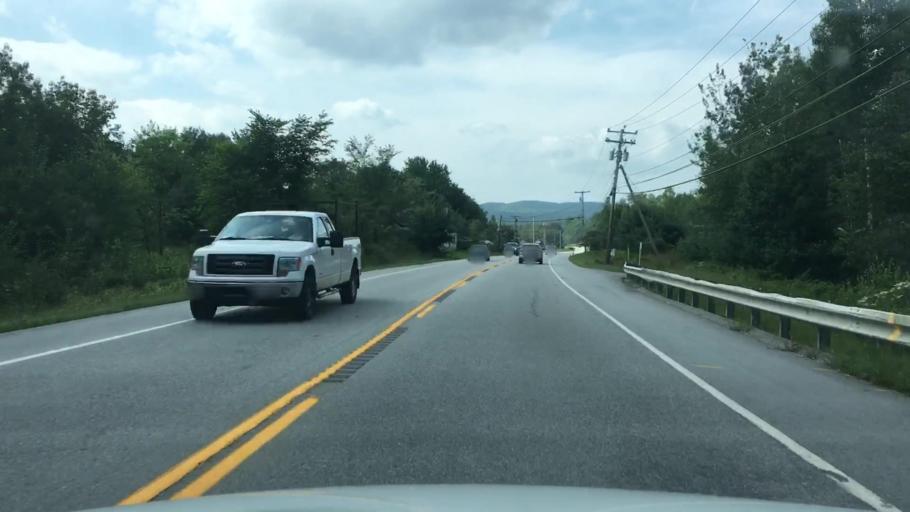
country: US
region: Maine
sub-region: Oxford County
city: Rumford
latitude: 44.5093
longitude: -70.5792
